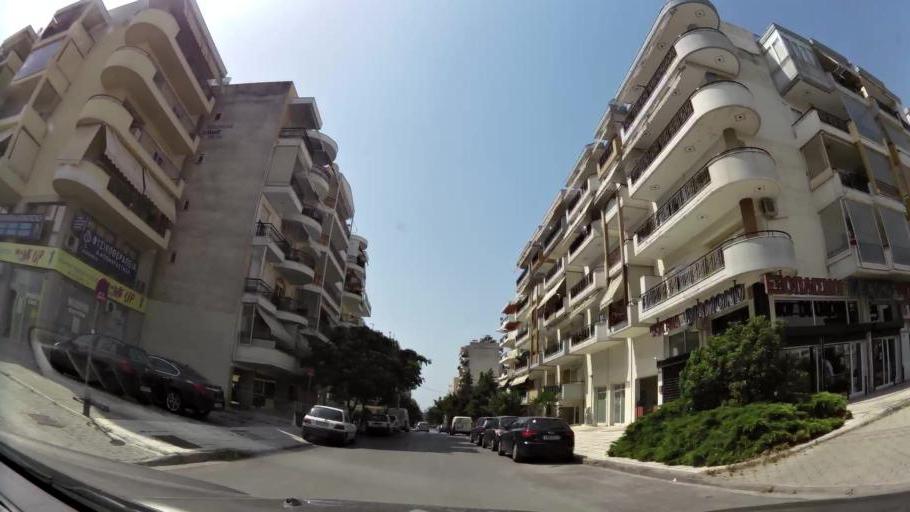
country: GR
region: Central Macedonia
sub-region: Nomos Thessalonikis
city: Evosmos
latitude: 40.6773
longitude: 22.9133
